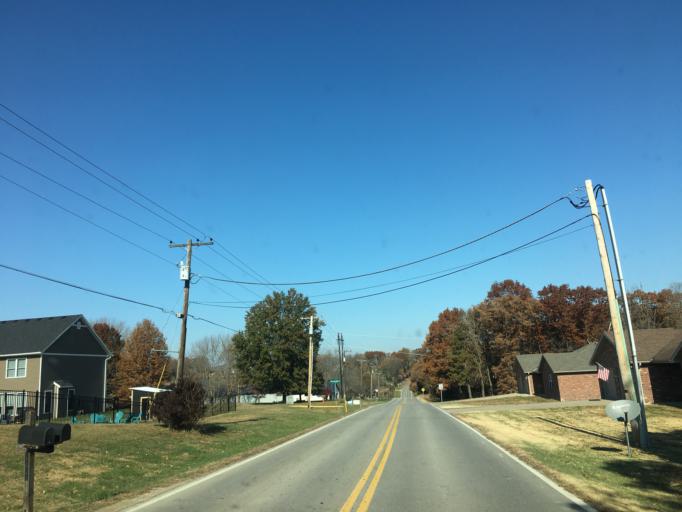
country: US
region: Missouri
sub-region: Cole County
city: Wardsville
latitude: 38.5121
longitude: -92.1760
